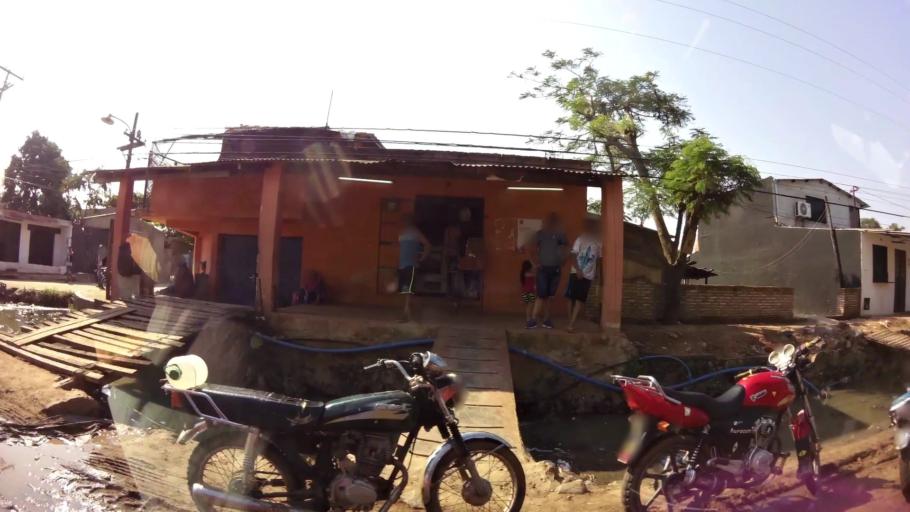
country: PY
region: Asuncion
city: Asuncion
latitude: -25.3244
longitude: -57.6417
